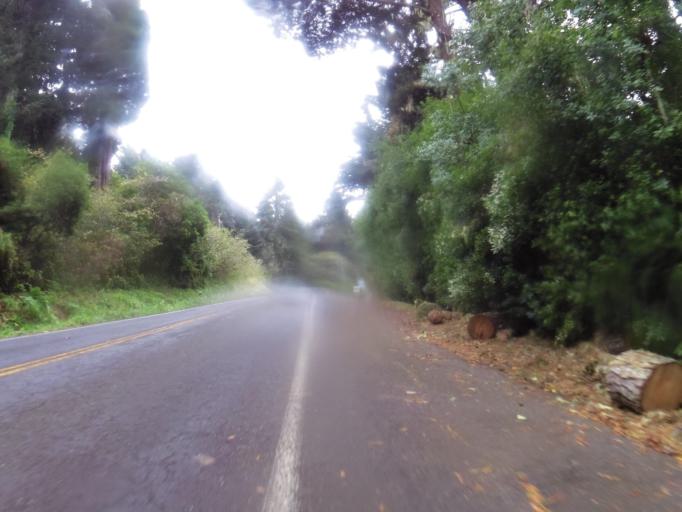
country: US
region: California
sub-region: Humboldt County
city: Westhaven-Moonstone
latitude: 41.1164
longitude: -124.1565
